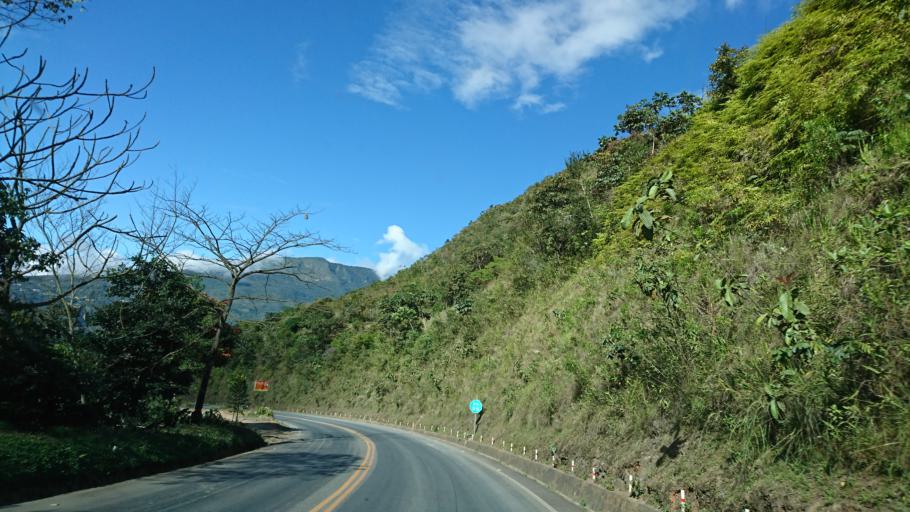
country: BO
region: La Paz
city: Coroico
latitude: -16.2053
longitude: -67.7750
